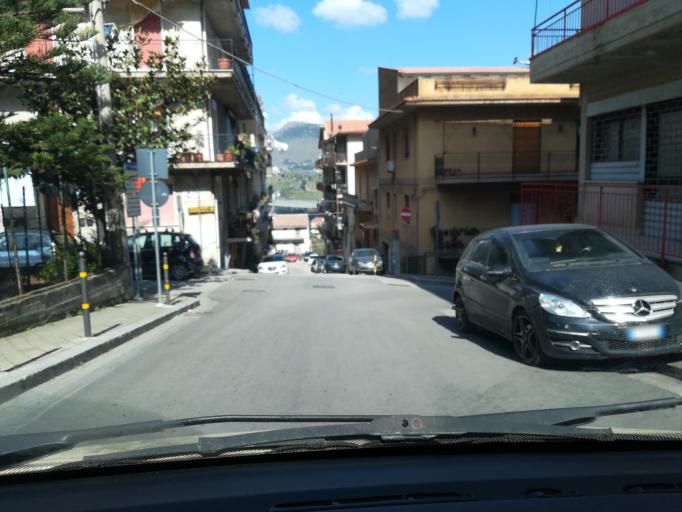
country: IT
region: Sicily
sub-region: Palermo
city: Altofonte
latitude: 38.0441
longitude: 13.2940
